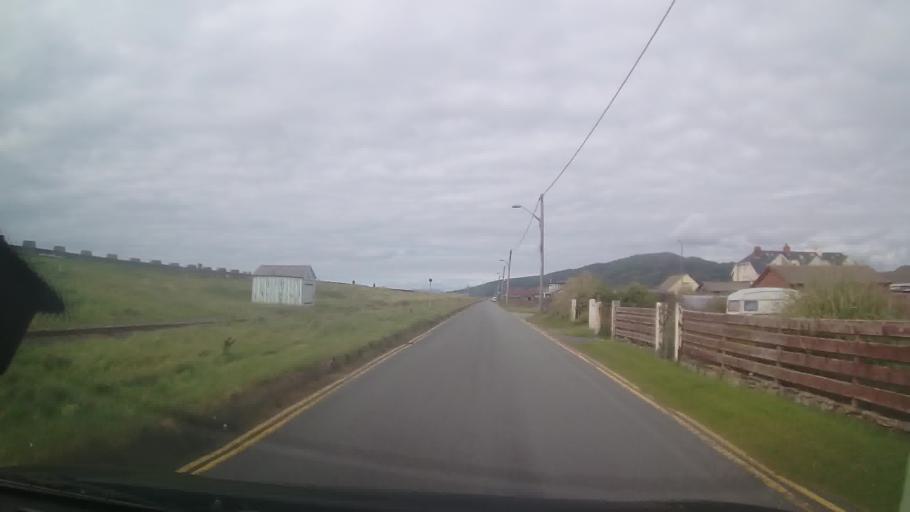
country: GB
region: Wales
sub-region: Gwynedd
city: Barmouth
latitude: 52.6979
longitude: -4.0568
